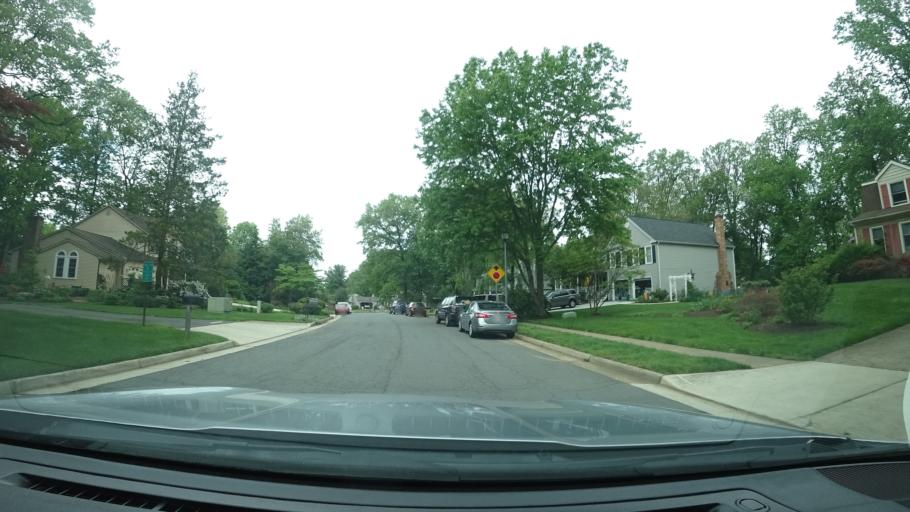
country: US
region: Virginia
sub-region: Fairfax County
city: Oak Hill
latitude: 38.9140
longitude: -77.3804
